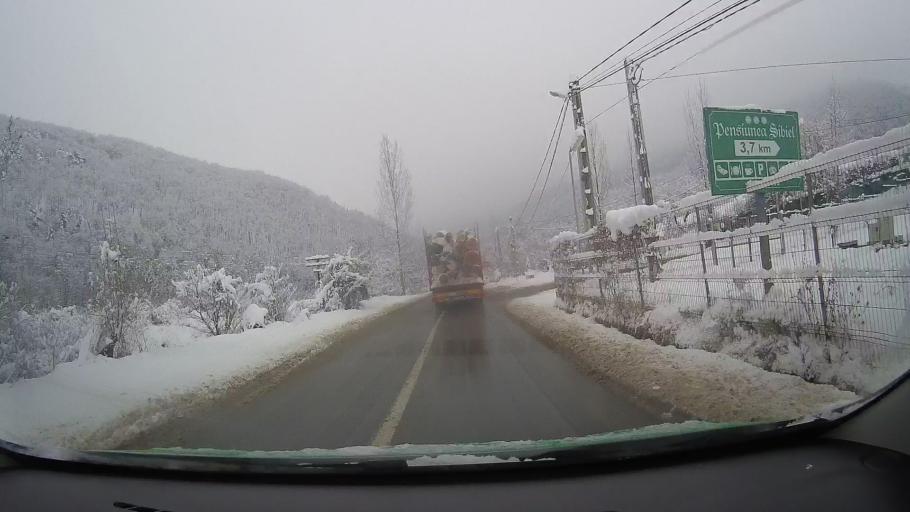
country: RO
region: Sibiu
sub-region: Comuna Orlat
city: Orlat
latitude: 45.7647
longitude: 23.9404
